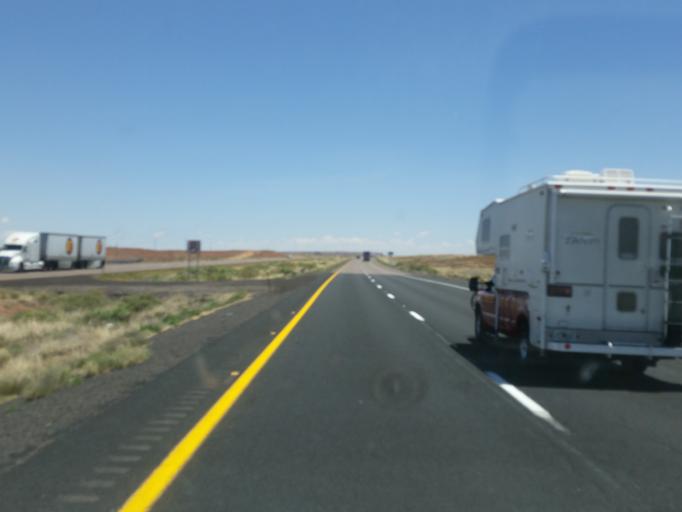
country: US
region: Arizona
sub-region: Coconino County
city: LeChee
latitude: 35.0933
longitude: -110.9251
